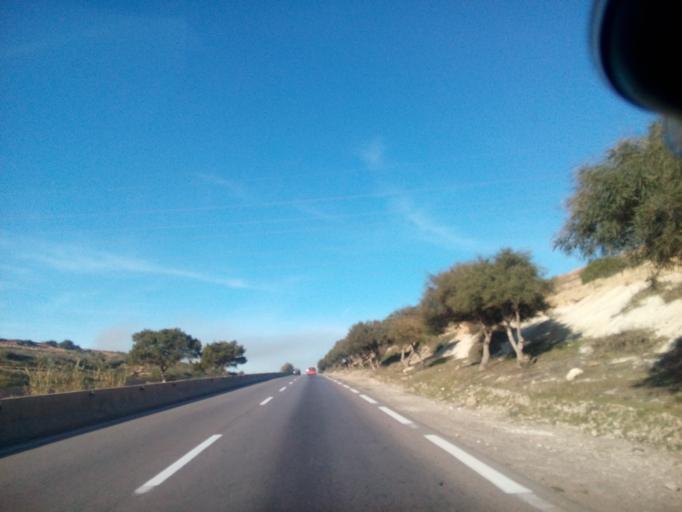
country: DZ
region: Oran
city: Ain el Bya
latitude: 35.7715
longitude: -0.2423
